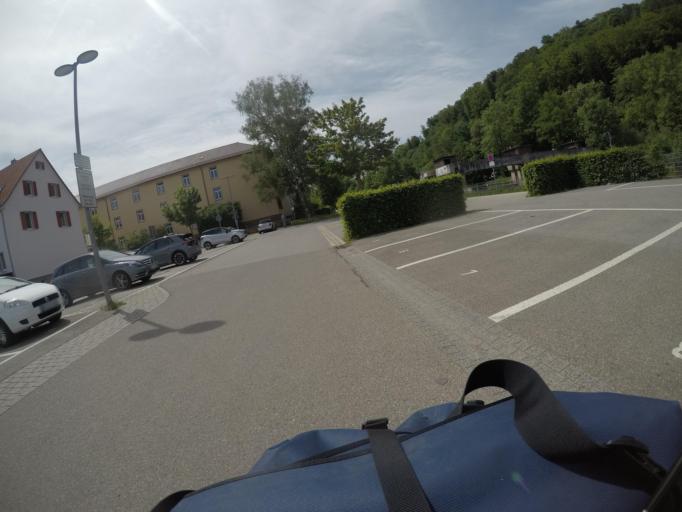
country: DE
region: Baden-Wuerttemberg
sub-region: Karlsruhe Region
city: Nagold
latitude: 48.5549
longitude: 8.7222
